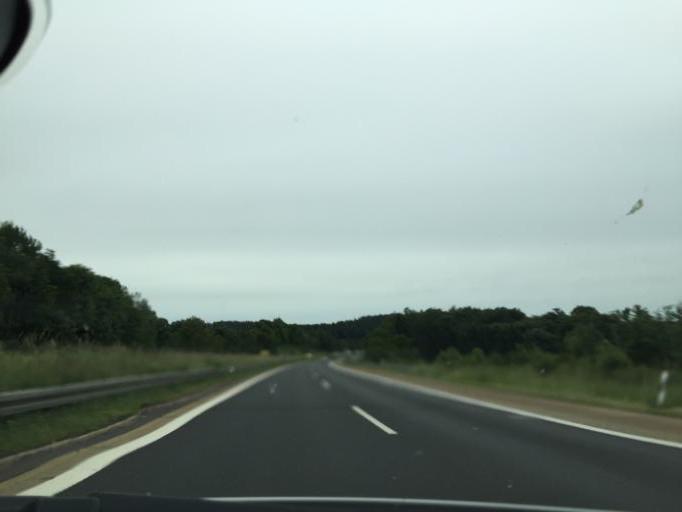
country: DE
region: Bavaria
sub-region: Regierungsbezirk Unterfranken
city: Schondra
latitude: 50.2800
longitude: 9.8665
